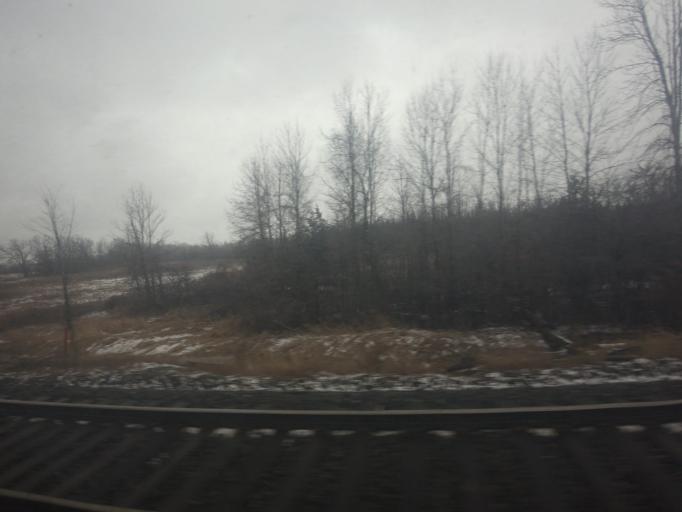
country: CA
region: Ontario
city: Belleville
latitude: 44.2040
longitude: -77.2635
